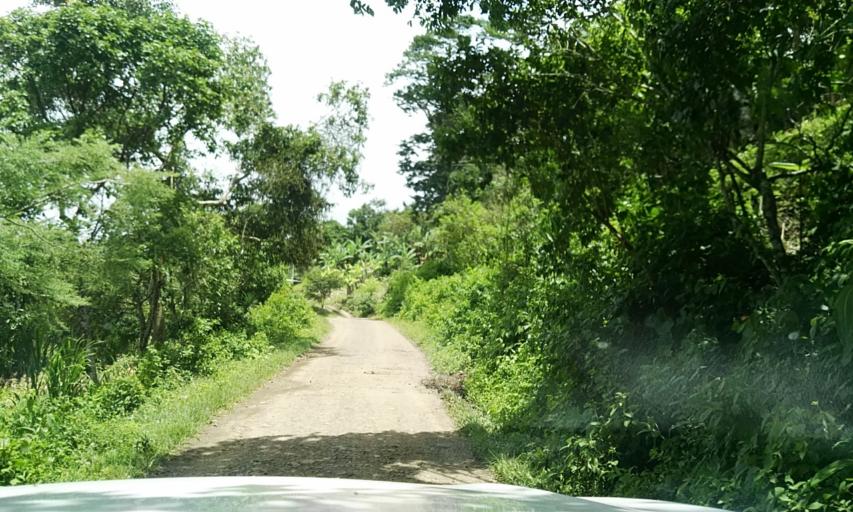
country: NI
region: Matagalpa
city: San Ramon
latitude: 12.9932
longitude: -85.8635
